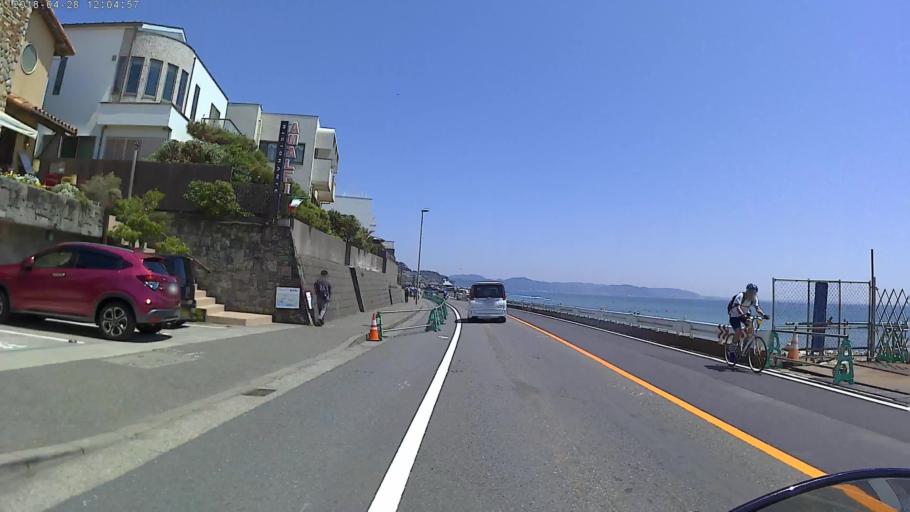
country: JP
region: Kanagawa
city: Kamakura
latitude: 35.3059
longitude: 139.5071
